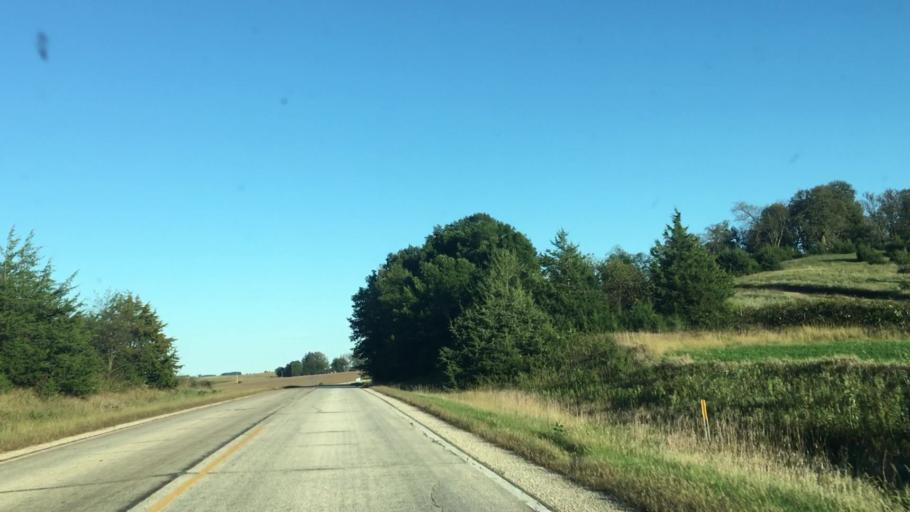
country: US
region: Minnesota
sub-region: Fillmore County
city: Chatfield
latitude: 43.8404
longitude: -92.0815
